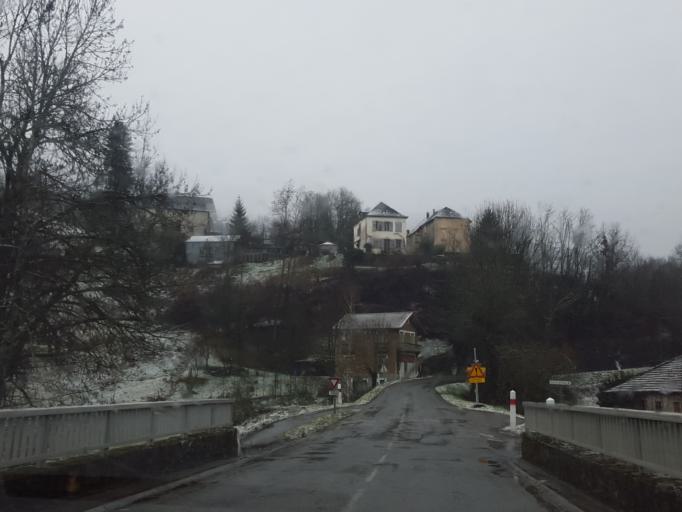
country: FR
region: Midi-Pyrenees
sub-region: Departement de l'Ariege
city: Montjoie-en-Couserans
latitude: 42.8922
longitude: 1.3492
